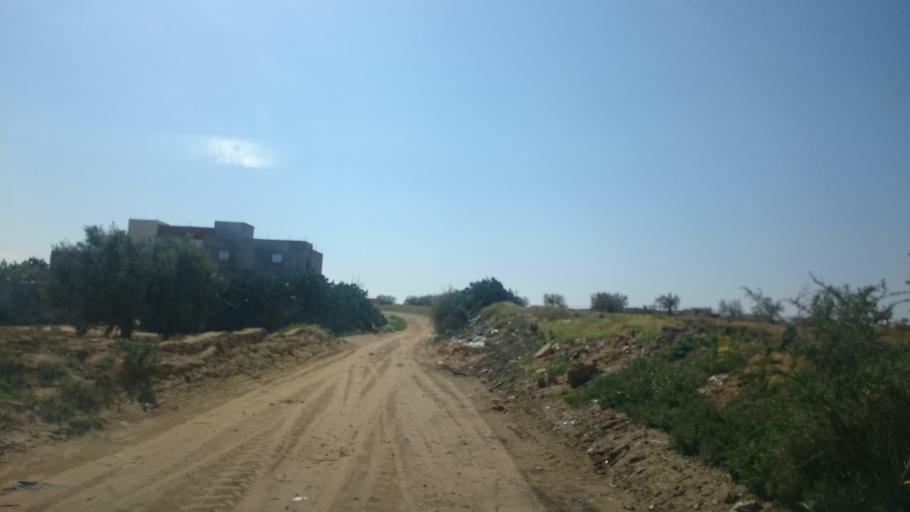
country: TN
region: Safaqis
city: Sfax
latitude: 34.7547
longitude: 10.5101
